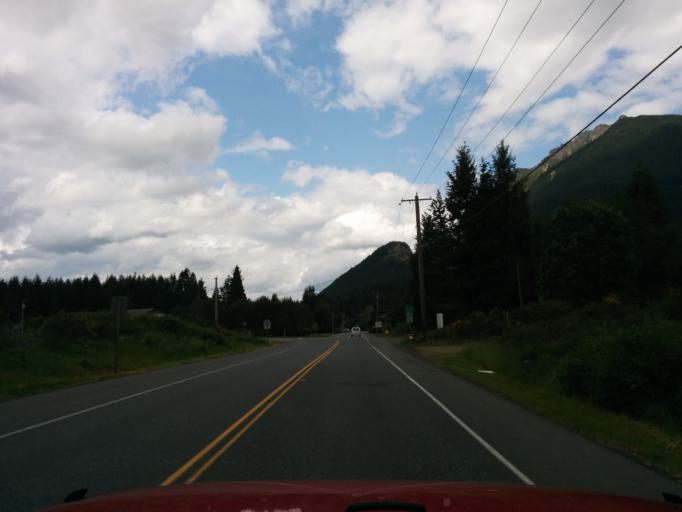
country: US
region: Washington
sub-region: King County
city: Tanner
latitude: 47.4784
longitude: -121.7584
